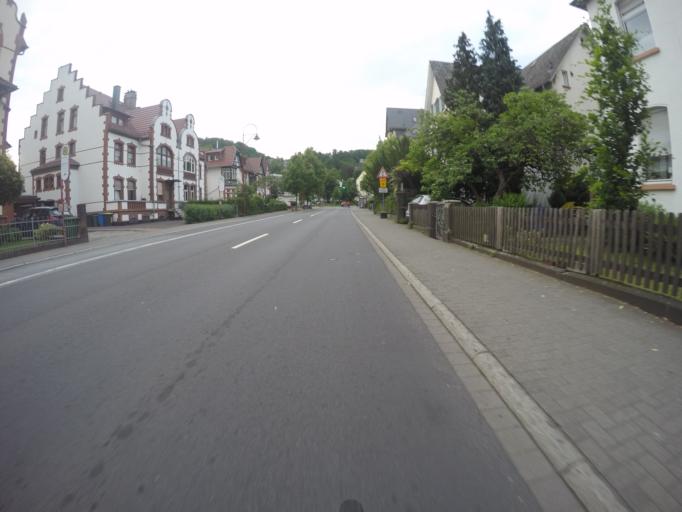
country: DE
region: Hesse
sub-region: Regierungsbezirk Giessen
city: Marburg an der Lahn
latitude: 50.8035
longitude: 8.7591
